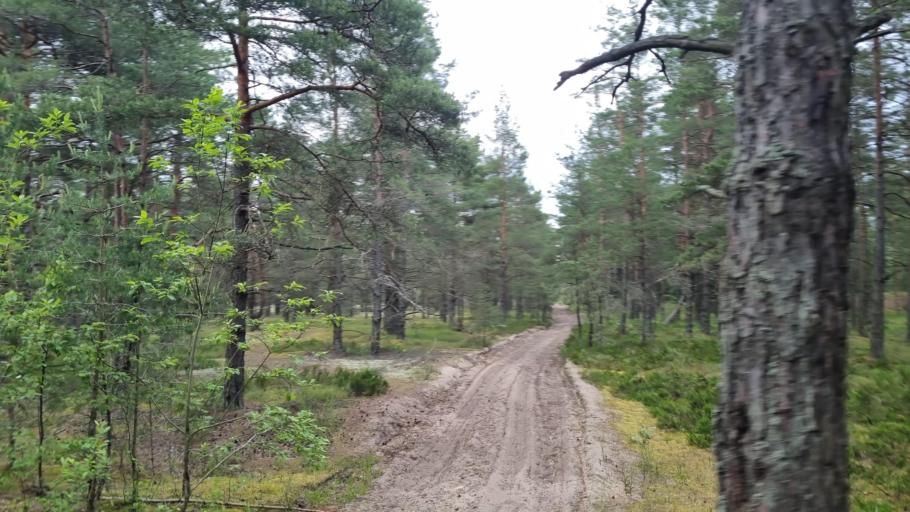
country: LV
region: Riga
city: Daugavgriva
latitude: 57.0162
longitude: 24.0284
